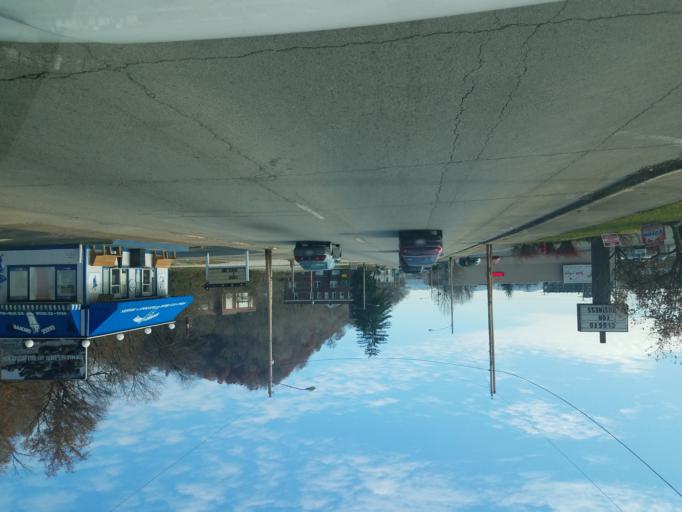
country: US
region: Ohio
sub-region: Scioto County
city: New Boston
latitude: 38.7551
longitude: -82.9329
